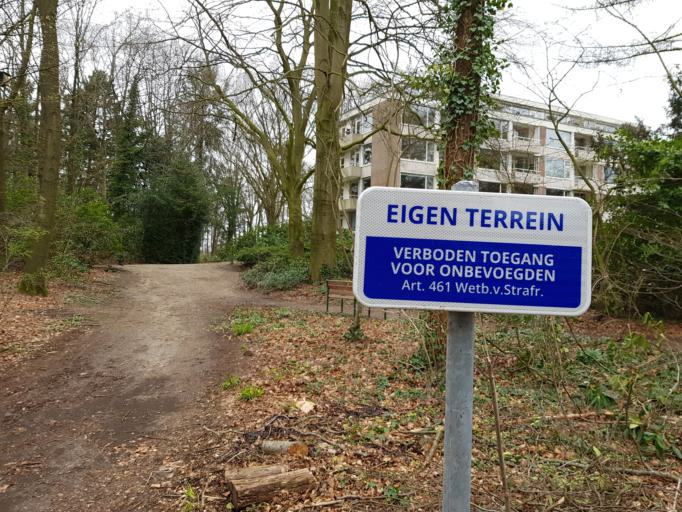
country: NL
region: Gelderland
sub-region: Gemeente Renkum
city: Oosterbeek
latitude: 51.9916
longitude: 5.8239
